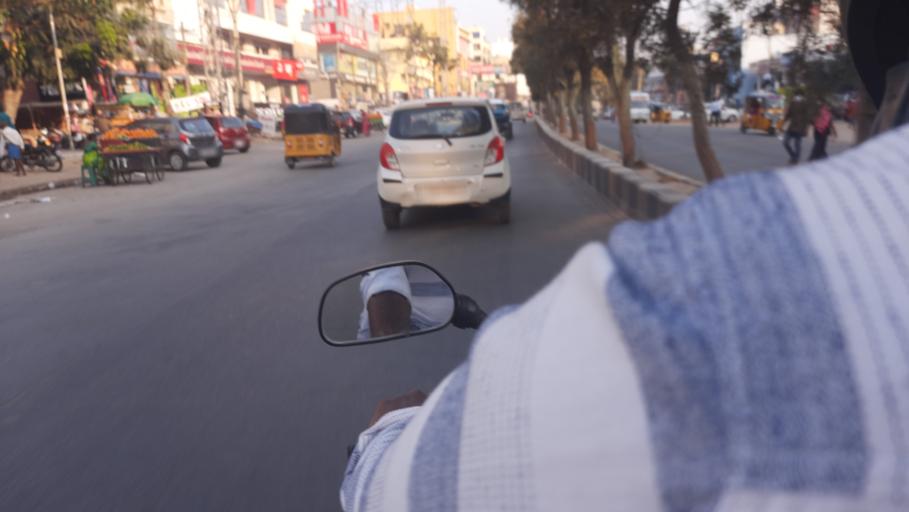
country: IN
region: Telangana
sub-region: Rangareddi
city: Secunderabad
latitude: 17.4811
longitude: 78.5556
